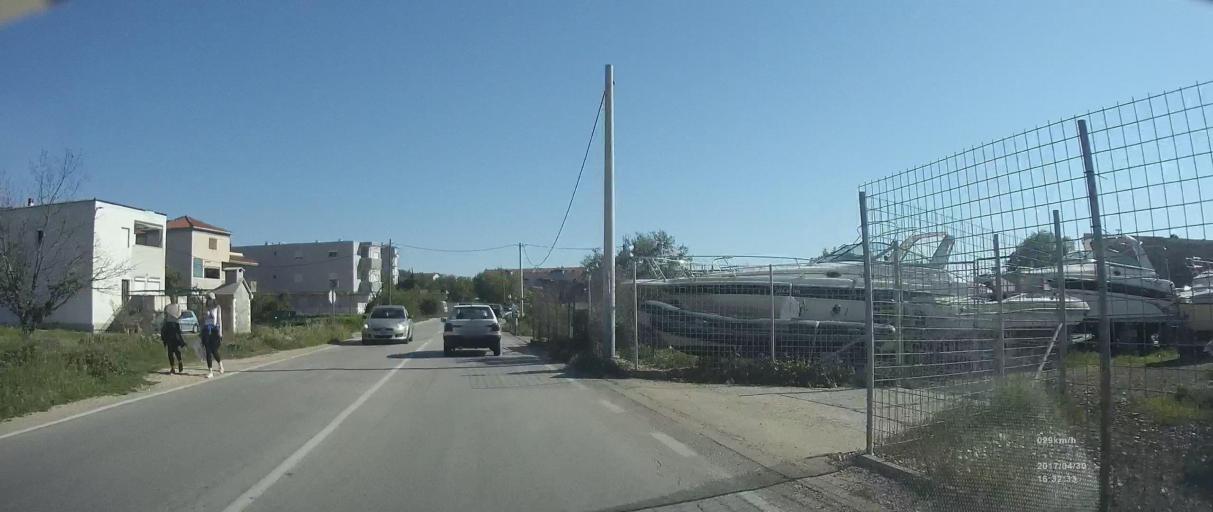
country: HR
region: Splitsko-Dalmatinska
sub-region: Grad Split
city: Stobrec
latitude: 43.5121
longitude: 16.5391
